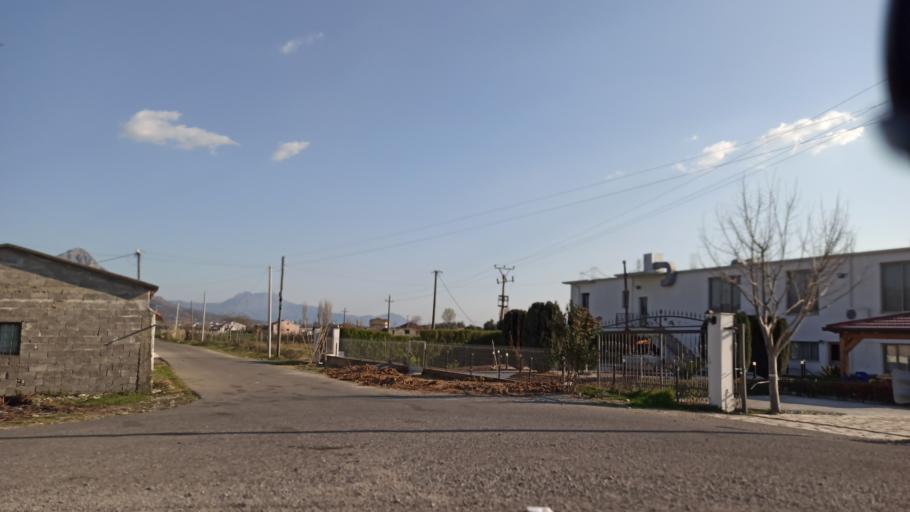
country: AL
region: Shkoder
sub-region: Rrethi i Shkodres
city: Vau i Dejes
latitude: 41.9940
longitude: 19.6095
